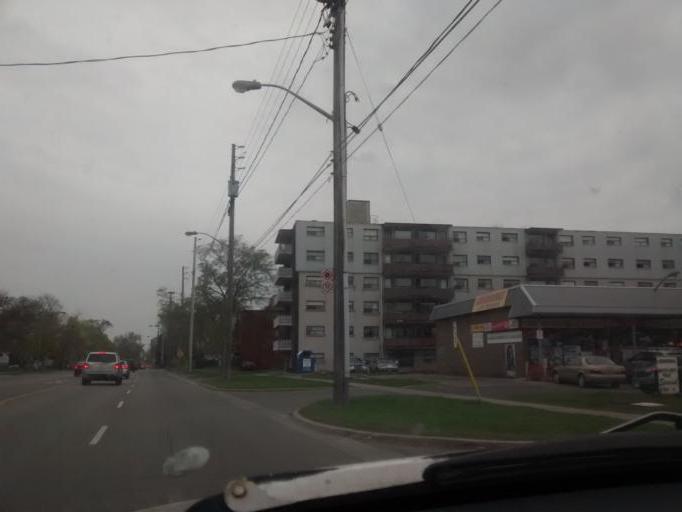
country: CA
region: Ontario
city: Burlington
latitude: 43.3375
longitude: -79.7863
